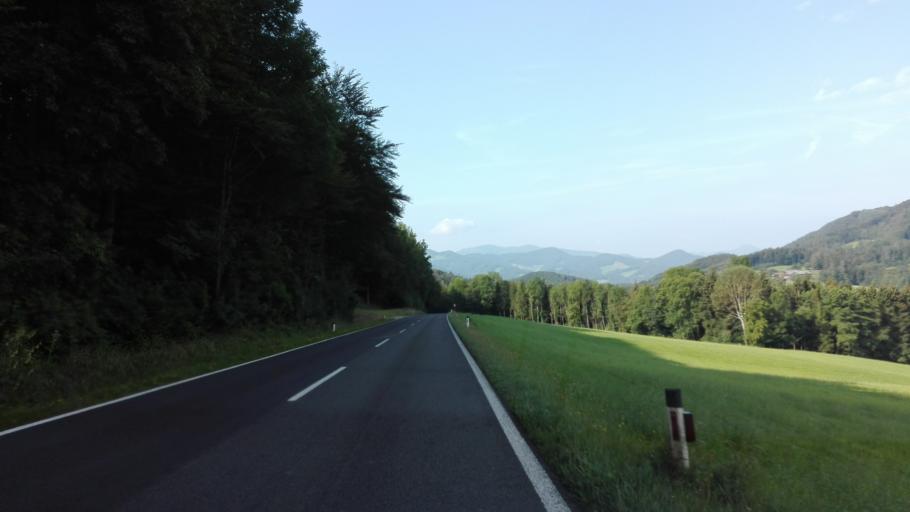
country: AT
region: Lower Austria
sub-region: Politischer Bezirk Lilienfeld
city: Rohrbach an der Goelsen
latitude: 48.0717
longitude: 15.7618
